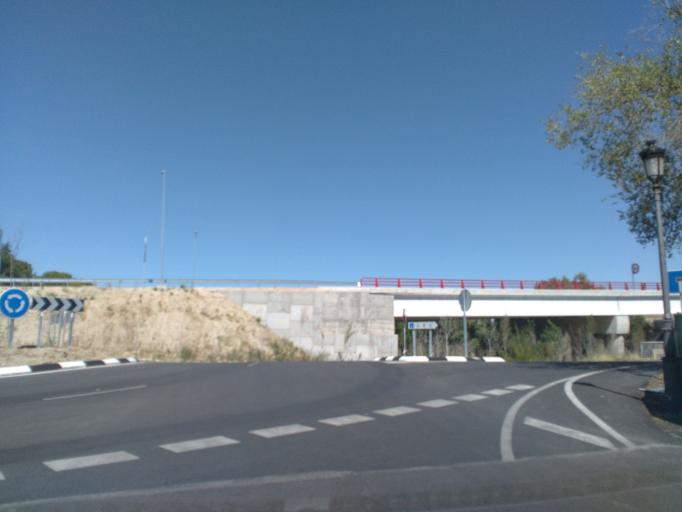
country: ES
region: Madrid
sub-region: Provincia de Madrid
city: Villanueva del Pardillo
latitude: 40.4843
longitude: -3.9377
